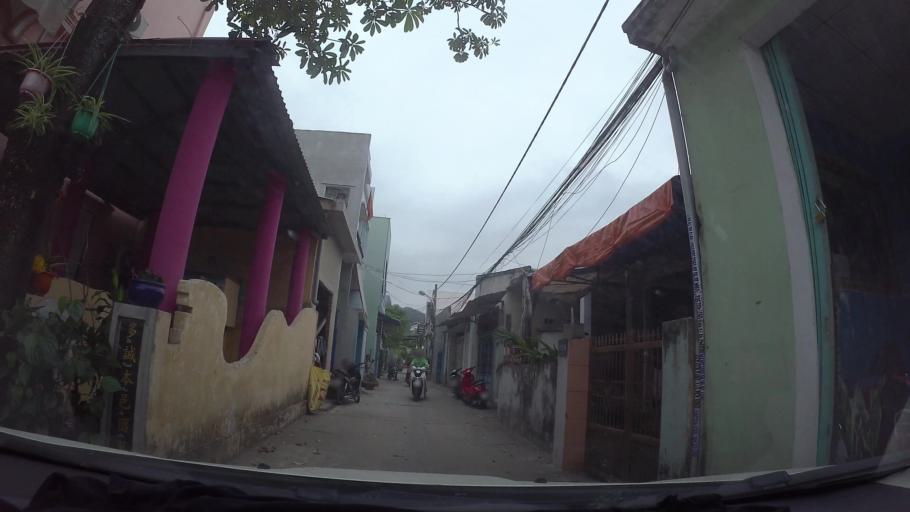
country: VN
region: Da Nang
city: Lien Chieu
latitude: 16.0736
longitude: 108.1452
